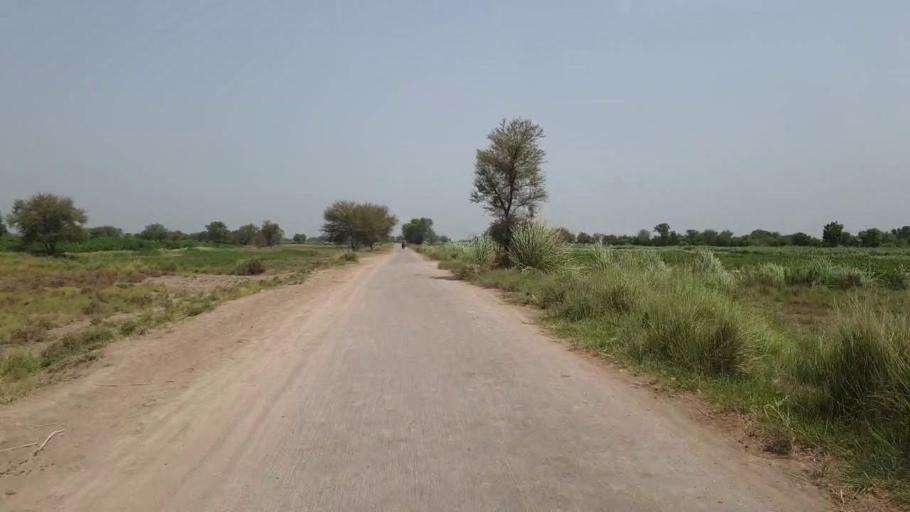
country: PK
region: Sindh
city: Nawabshah
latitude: 26.2620
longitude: 68.3185
